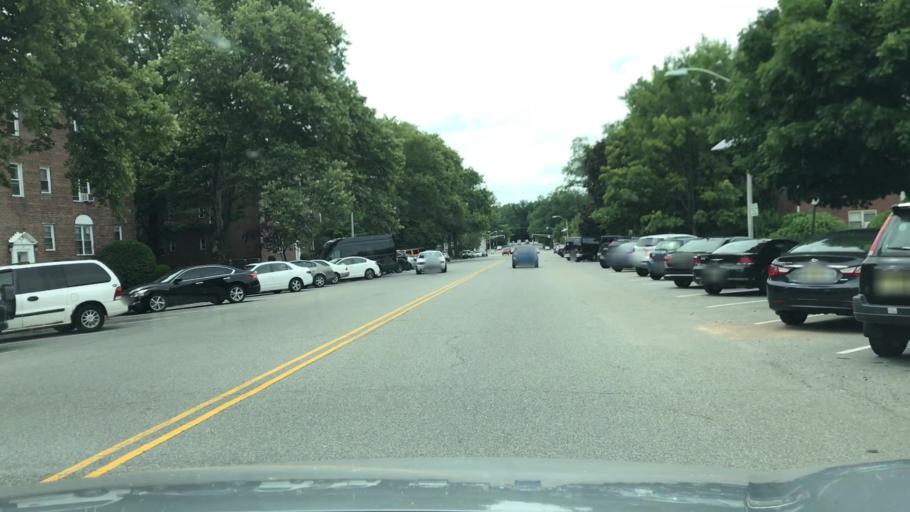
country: US
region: New Jersey
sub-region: Bergen County
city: Teaneck
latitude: 40.9016
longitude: -74.0011
